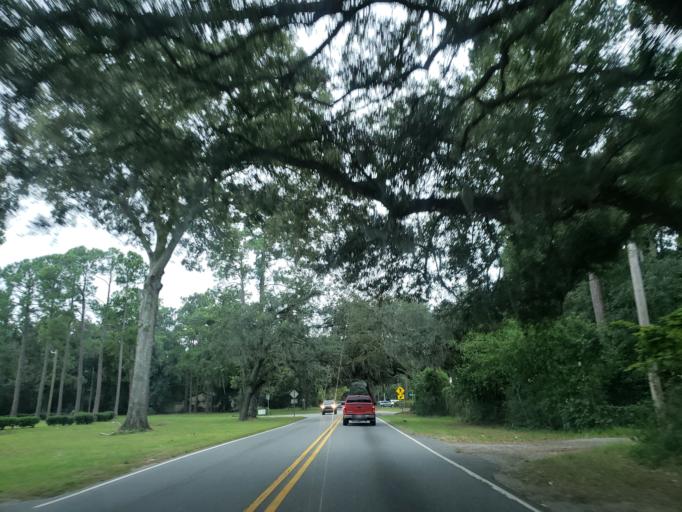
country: US
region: Georgia
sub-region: Chatham County
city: Thunderbolt
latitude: 32.0171
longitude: -81.0763
